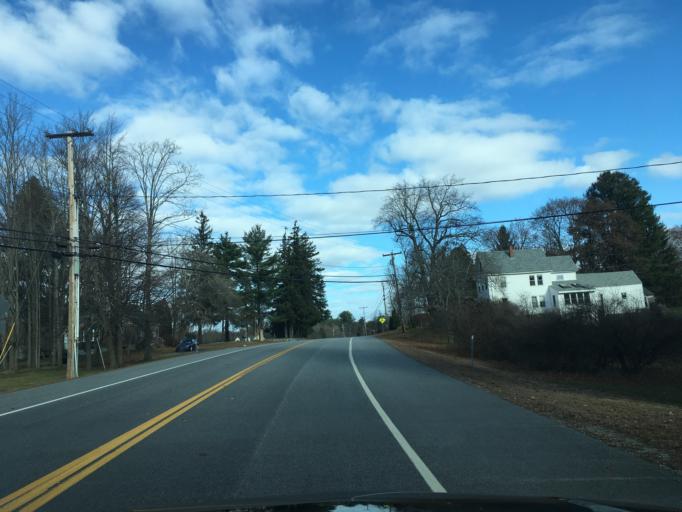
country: US
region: New Hampshire
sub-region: Rockingham County
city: Stratham Station
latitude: 43.0269
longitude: -70.9110
